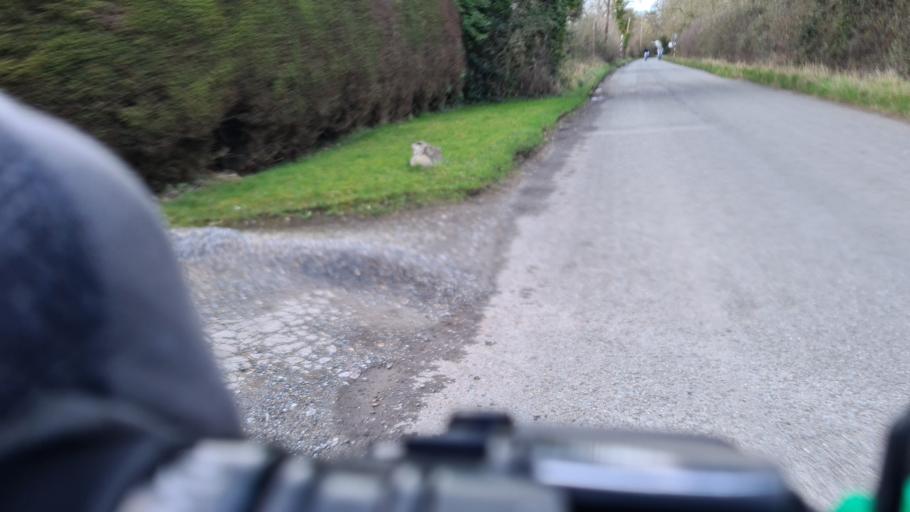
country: IE
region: Leinster
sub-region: Kildare
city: Maynooth
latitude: 53.3483
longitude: -6.5824
